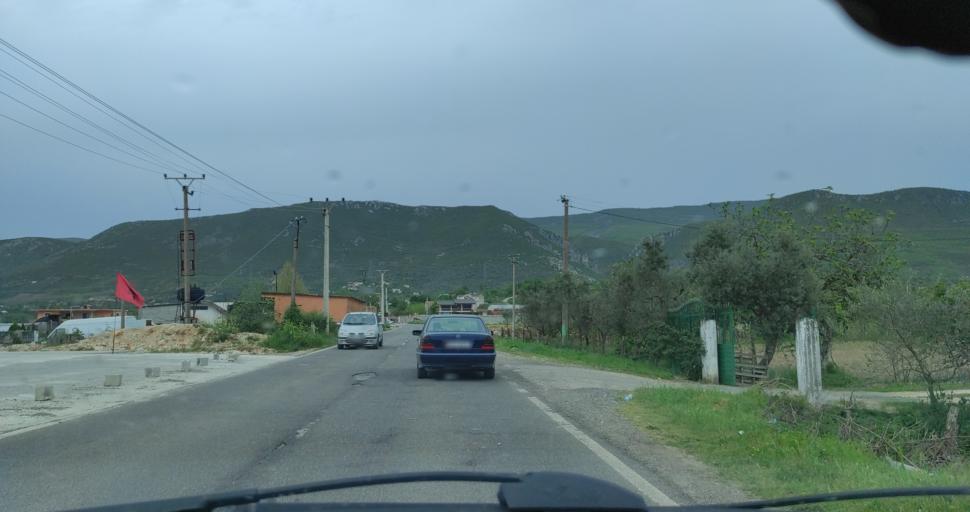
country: AL
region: Lezhe
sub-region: Rrethi i Kurbinit
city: Lac
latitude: 41.6050
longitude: 19.7089
